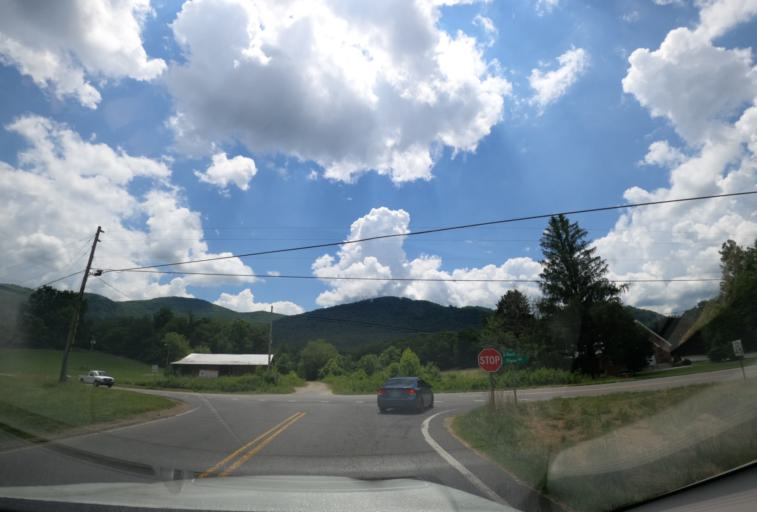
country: US
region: North Carolina
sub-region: Haywood County
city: Waynesville
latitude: 35.4765
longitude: -82.9627
